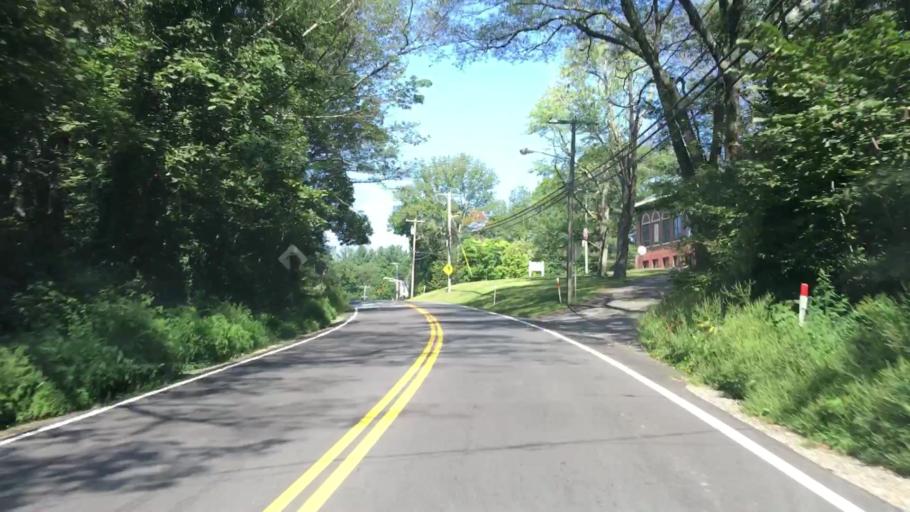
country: US
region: New Hampshire
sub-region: Rockingham County
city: East Kingston
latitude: 42.9242
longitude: -71.0111
